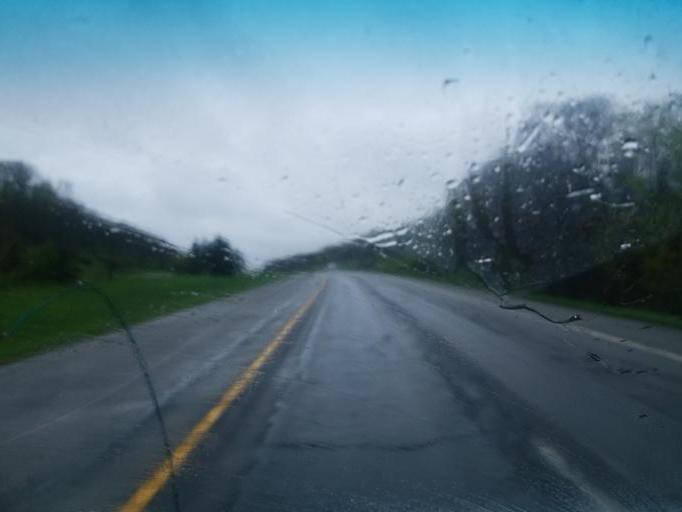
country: US
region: New York
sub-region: Chautauqua County
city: Lakewood
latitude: 42.1343
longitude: -79.3318
